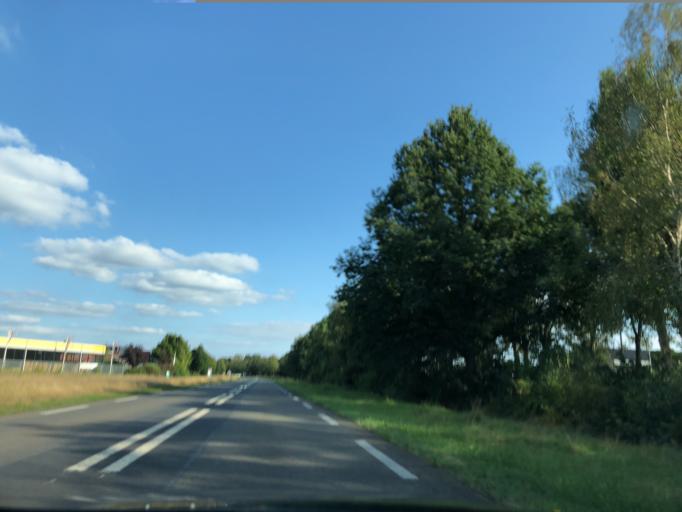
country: NL
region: Groningen
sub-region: Gemeente Stadskanaal
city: Stadskanaal
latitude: 52.9763
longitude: 6.9482
